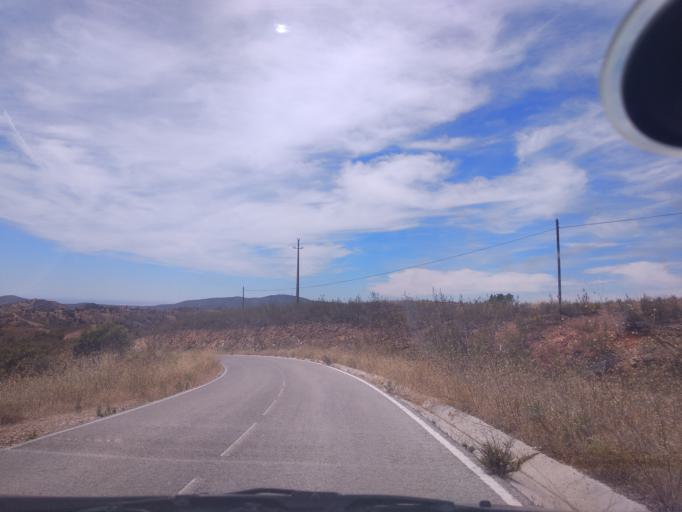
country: PT
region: Faro
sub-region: Sao Bras de Alportel
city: Sao Bras de Alportel
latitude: 37.1897
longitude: -7.7971
